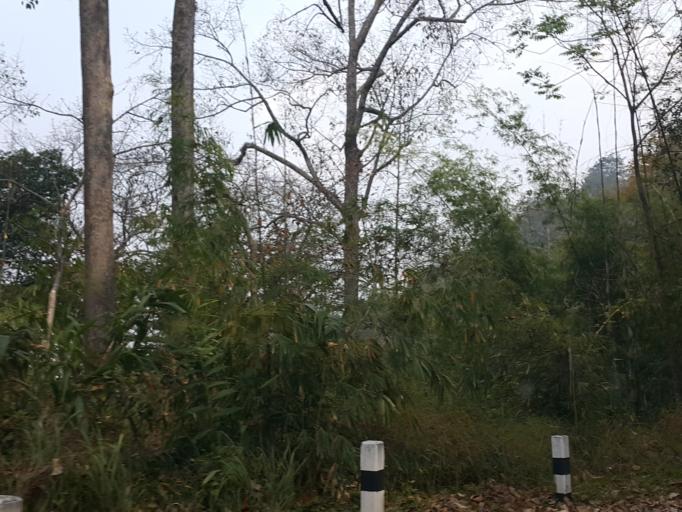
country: TH
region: Chiang Mai
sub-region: Amphoe Chiang Dao
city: Chiang Dao
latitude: 19.4121
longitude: 98.8871
